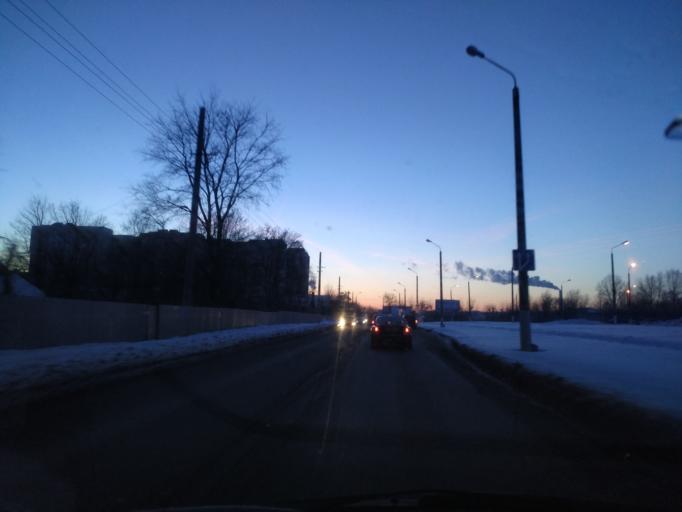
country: BY
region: Mogilev
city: Mahilyow
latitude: 53.8839
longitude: 30.3295
